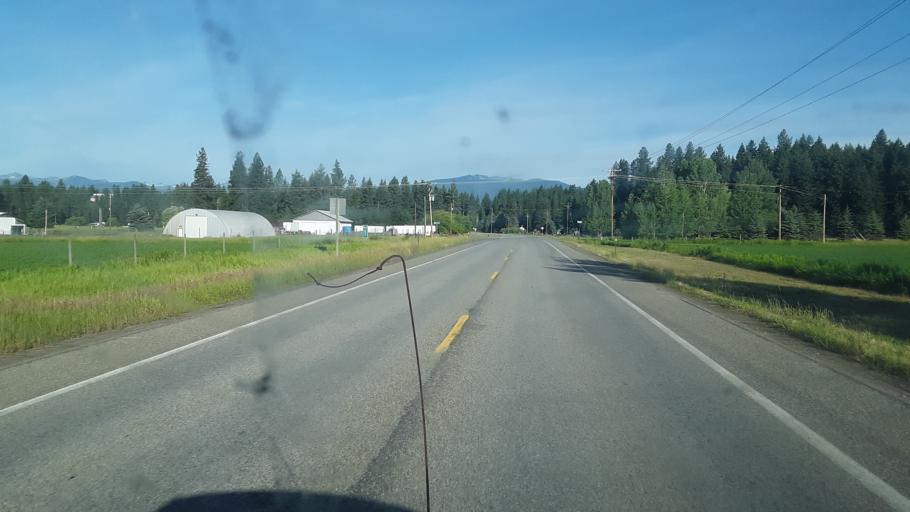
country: US
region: Idaho
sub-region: Boundary County
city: Bonners Ferry
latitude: 48.7310
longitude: -116.2417
